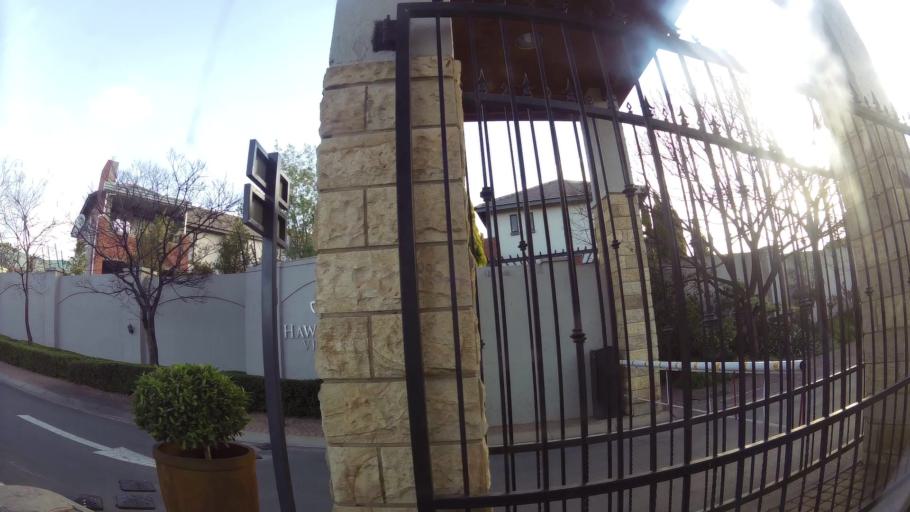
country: ZA
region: Gauteng
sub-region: City of Johannesburg Metropolitan Municipality
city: Diepsloot
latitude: -26.0147
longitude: 28.0058
